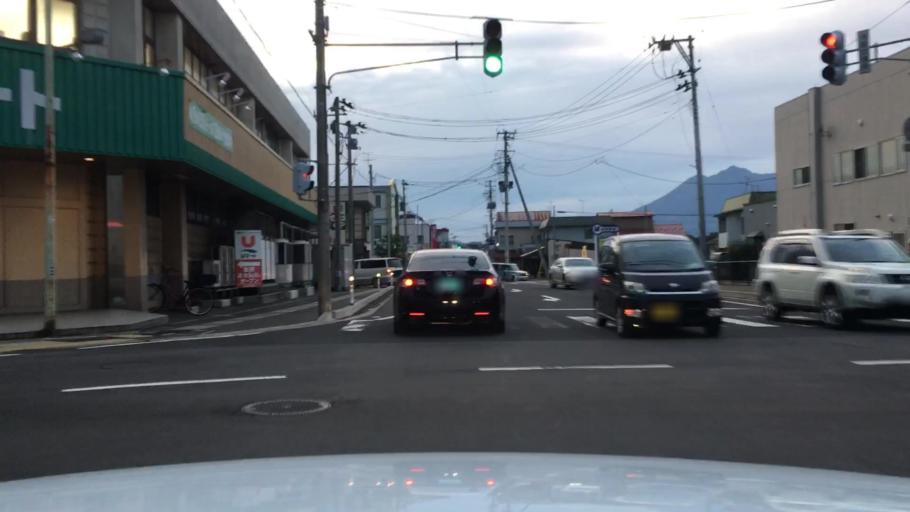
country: JP
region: Aomori
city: Hirosaki
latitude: 40.5918
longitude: 140.4733
